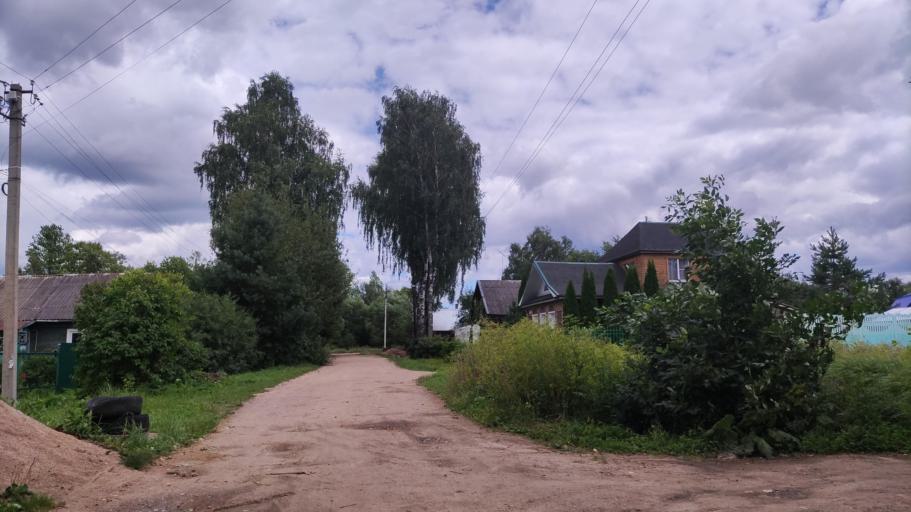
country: RU
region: Tverskaya
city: Rzhev
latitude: 56.2468
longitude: 34.3026
